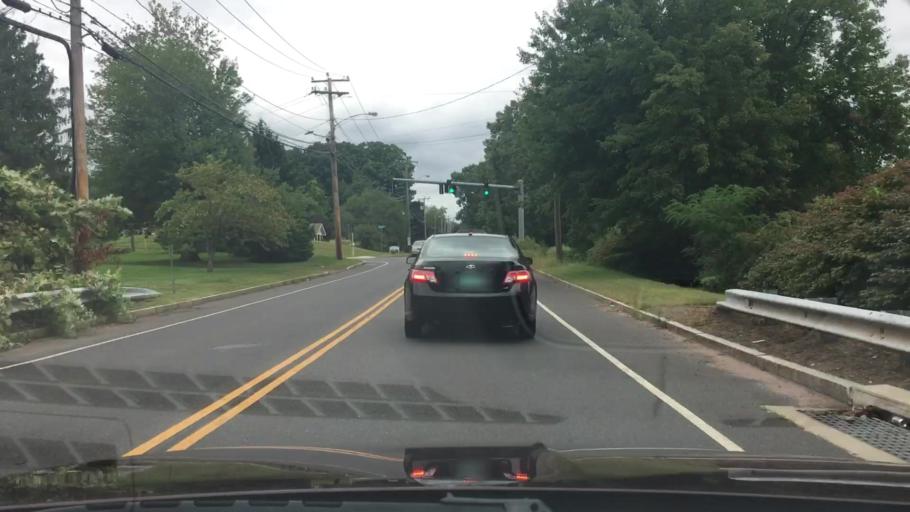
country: US
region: Connecticut
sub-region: Hartford County
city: Manchester
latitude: 41.8027
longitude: -72.5346
